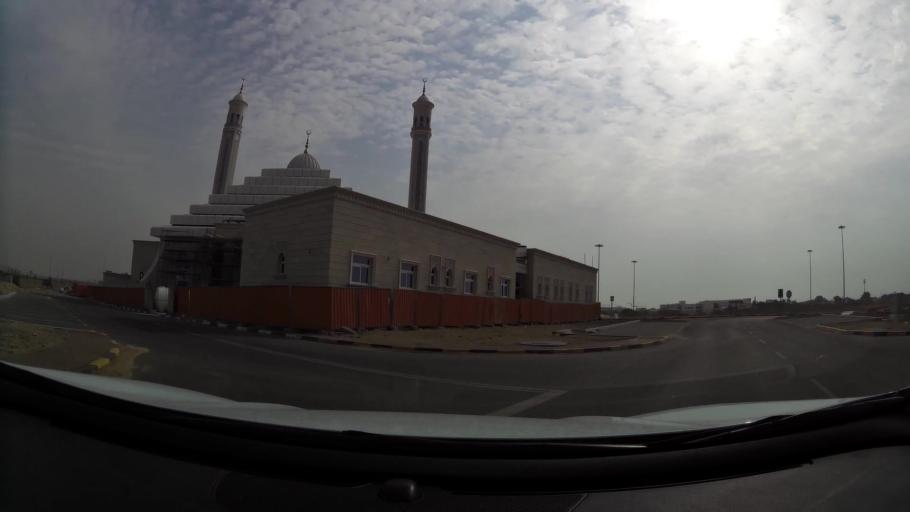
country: AE
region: Abu Dhabi
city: Abu Dhabi
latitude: 24.6842
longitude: 54.7692
